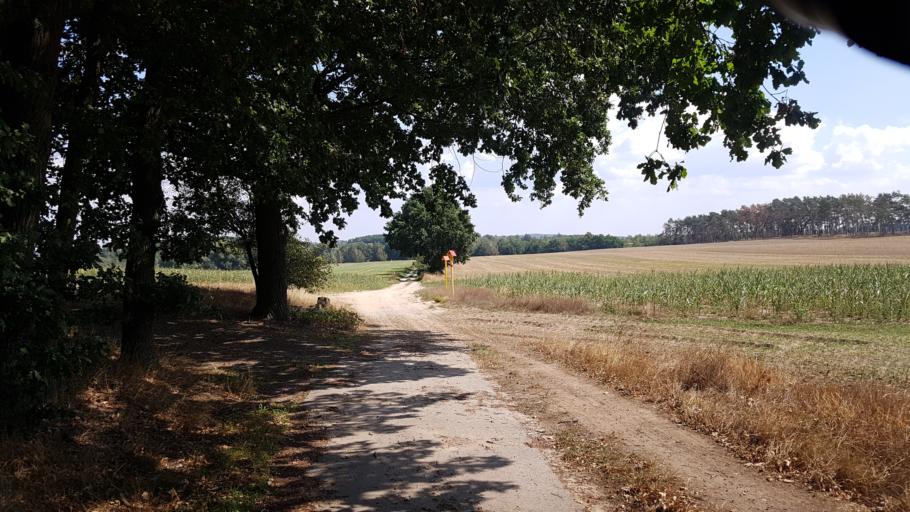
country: DE
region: Brandenburg
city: Hirschfeld
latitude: 51.3812
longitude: 13.6309
